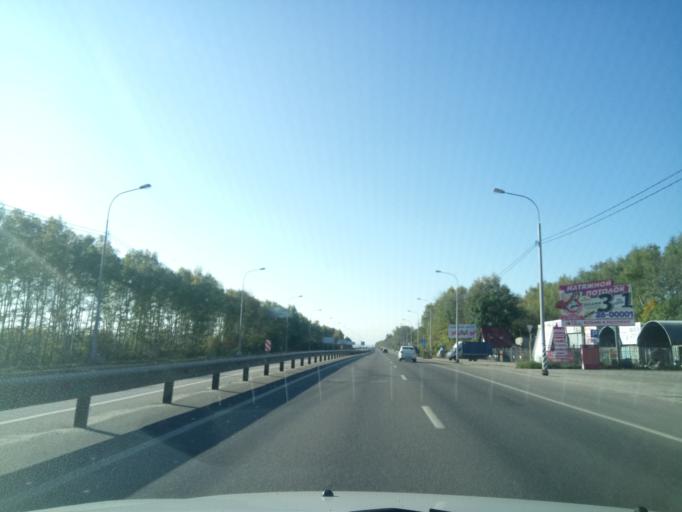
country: RU
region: Nizjnij Novgorod
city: Nizhniy Novgorod
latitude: 56.2117
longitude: 43.9288
